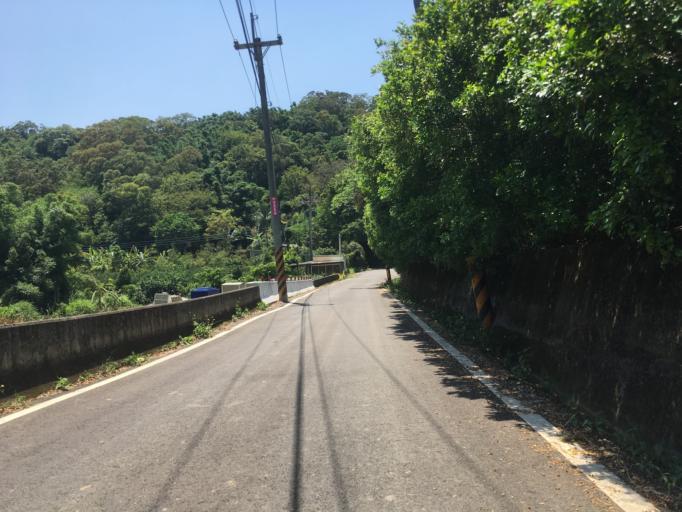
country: TW
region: Taiwan
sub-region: Hsinchu
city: Hsinchu
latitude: 24.7306
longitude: 120.9817
